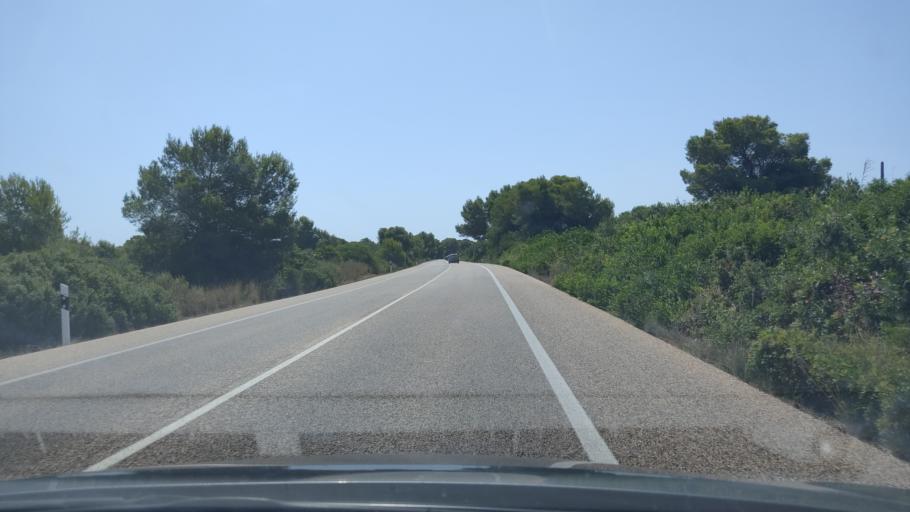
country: ES
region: Valencia
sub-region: Provincia de Valencia
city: Sollana
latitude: 39.3335
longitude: -0.3143
